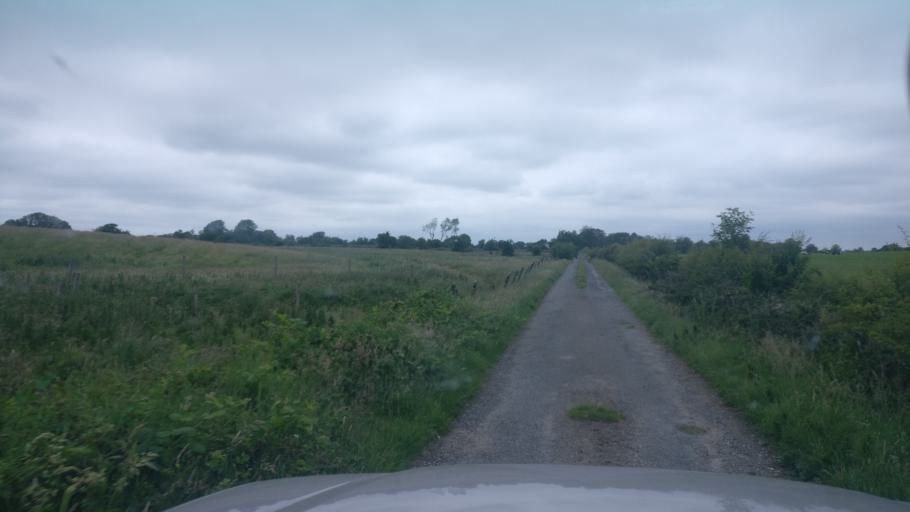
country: IE
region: Connaught
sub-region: County Galway
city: Ballinasloe
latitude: 53.2980
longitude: -8.3627
